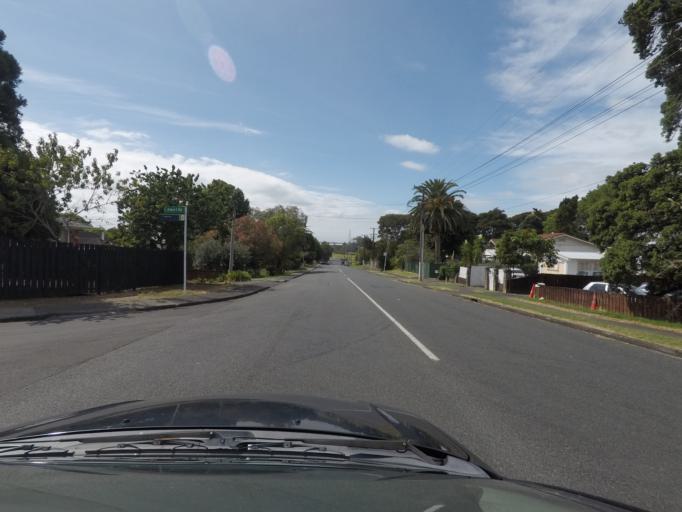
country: NZ
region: Auckland
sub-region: Auckland
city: Rosebank
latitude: -36.8967
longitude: 174.6683
